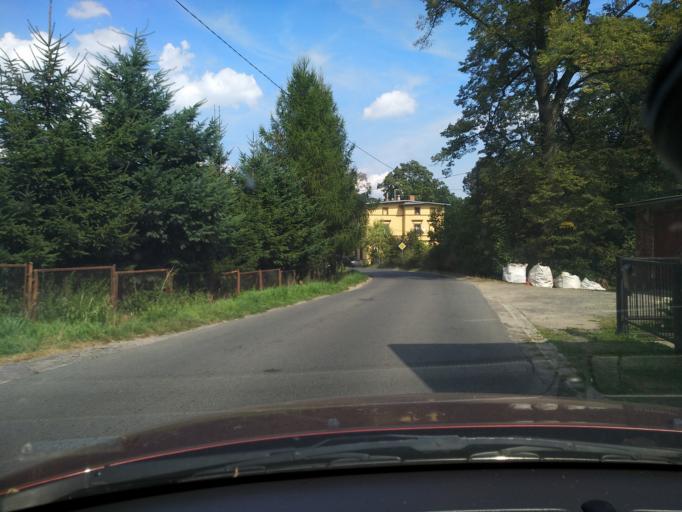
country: PL
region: Lower Silesian Voivodeship
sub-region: Powiat jeleniogorski
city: Stara Kamienica
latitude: 50.9121
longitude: 15.5706
